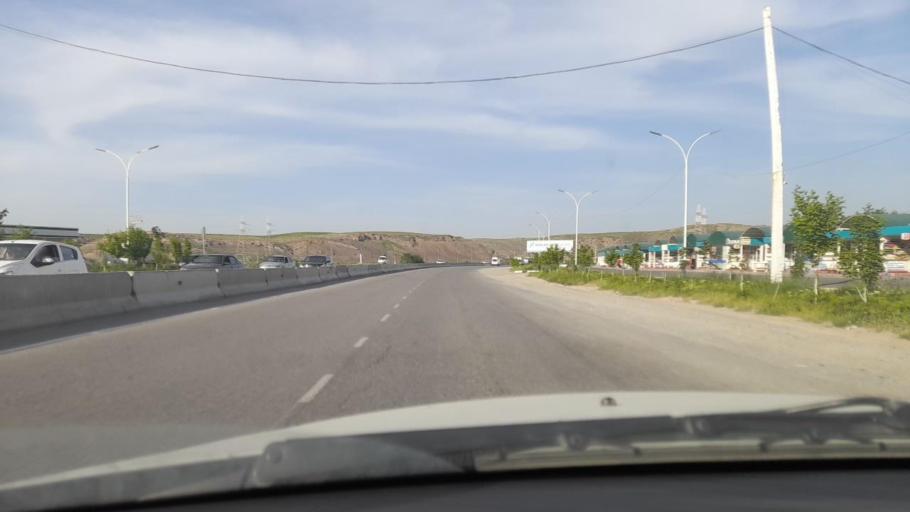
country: UZ
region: Jizzax
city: Jizzax
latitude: 40.0347
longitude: 67.6278
